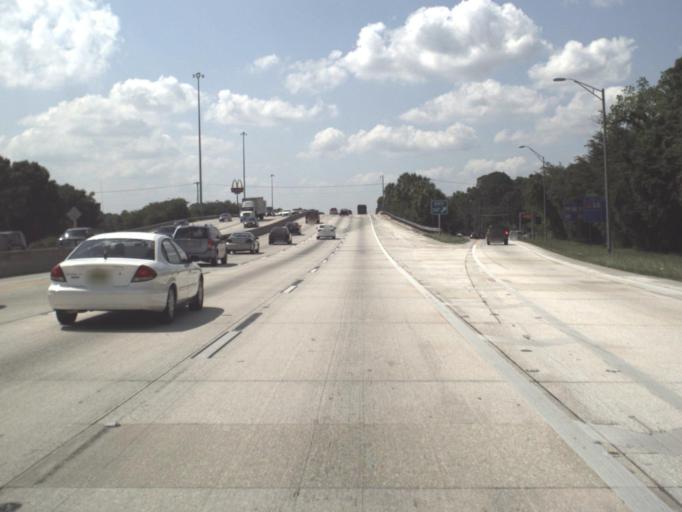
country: US
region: Florida
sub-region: Duval County
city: Jacksonville
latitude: 30.2887
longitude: -81.6275
